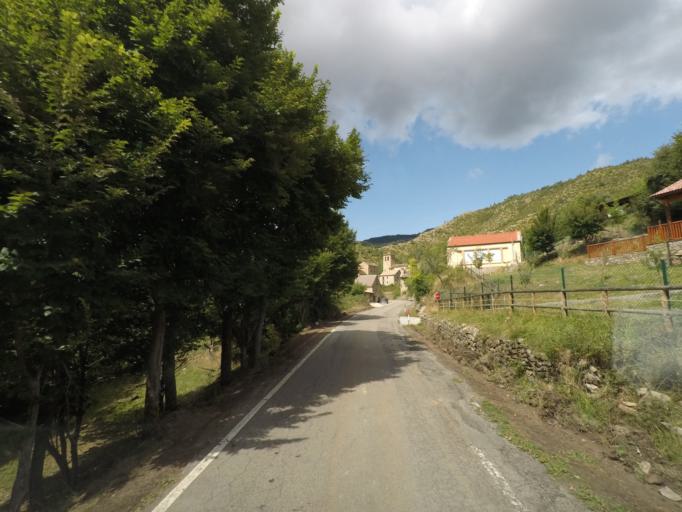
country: ES
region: Aragon
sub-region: Provincia de Huesca
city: Fiscal
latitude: 42.4124
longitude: -0.1179
